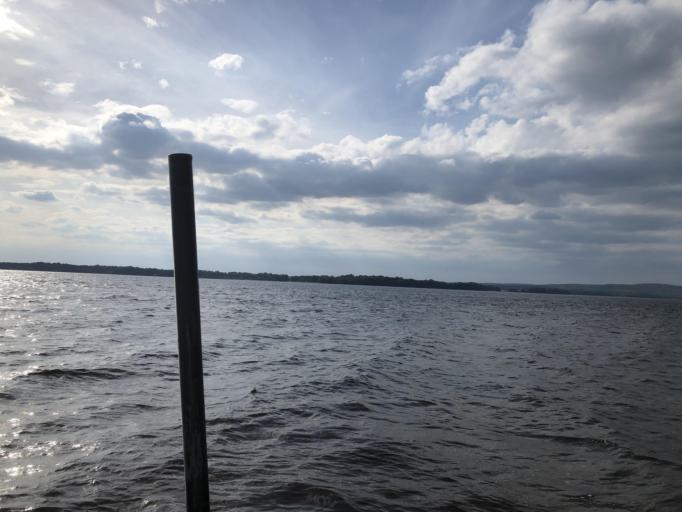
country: SE
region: Skane
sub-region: Bromolla Kommun
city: Bromoella
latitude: 56.0873
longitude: 14.4619
